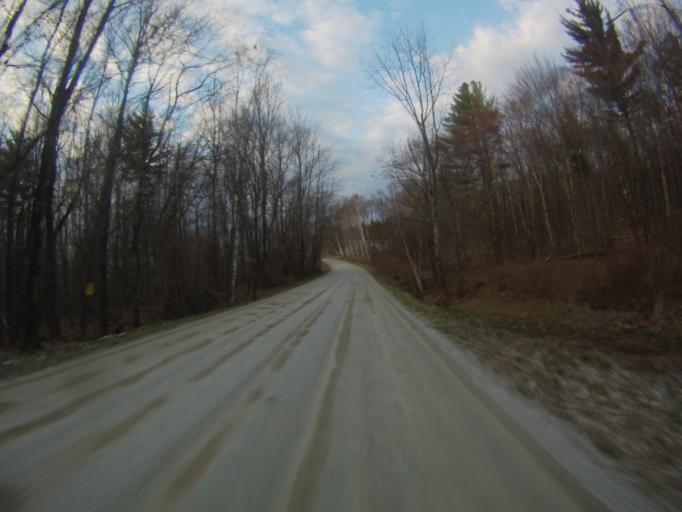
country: US
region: Vermont
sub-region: Rutland County
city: Brandon
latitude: 43.8766
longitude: -73.0132
